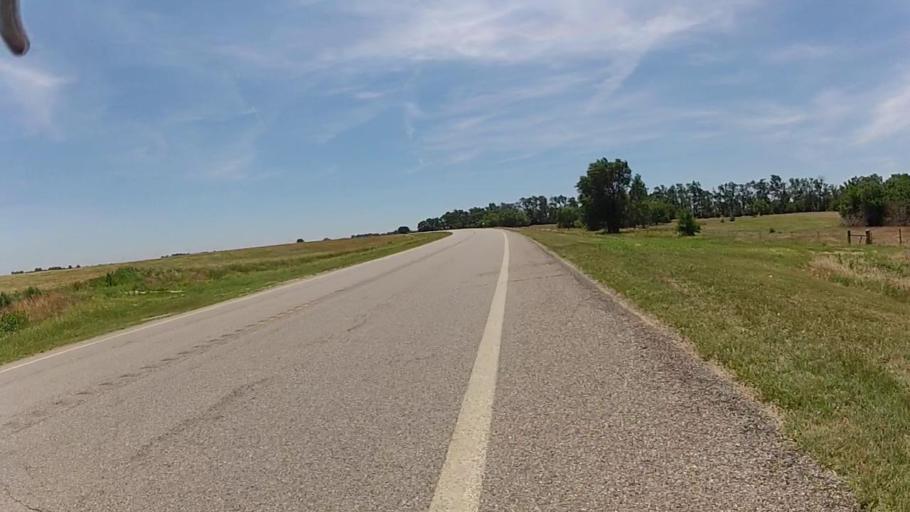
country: US
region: Kansas
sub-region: Barber County
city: Medicine Lodge
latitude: 37.2562
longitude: -98.5232
